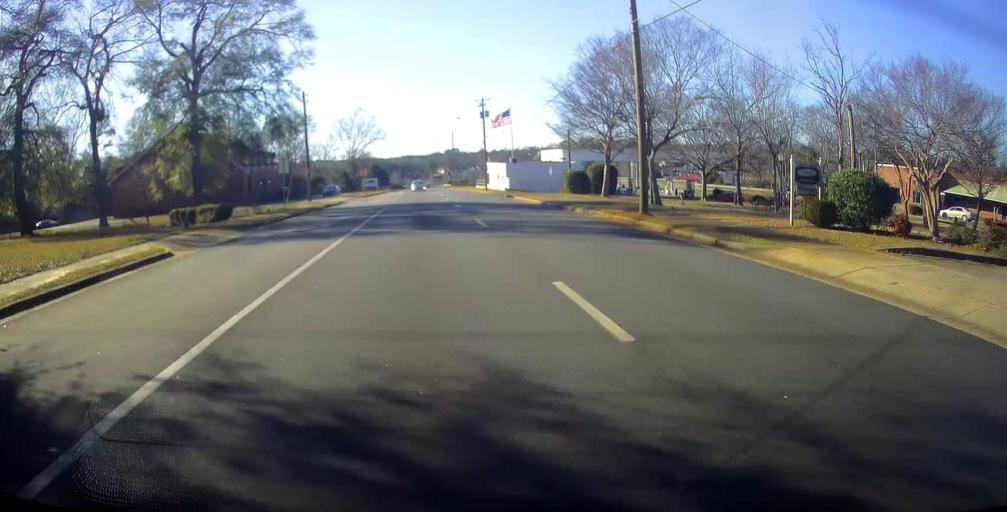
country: US
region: Georgia
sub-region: Sumter County
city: Americus
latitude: 32.0728
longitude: -84.2391
